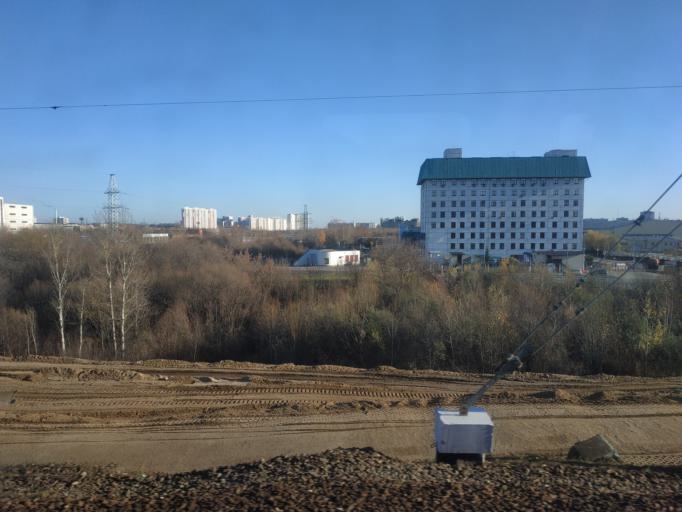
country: RU
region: Moscow
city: Nagornyy
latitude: 55.6390
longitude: 37.6253
